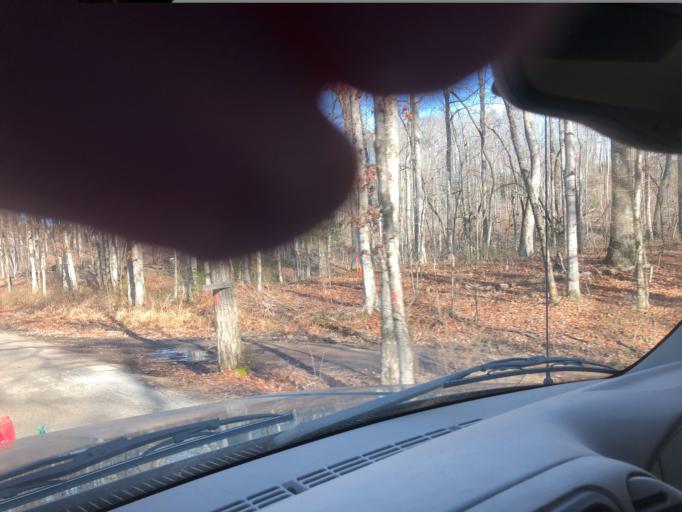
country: US
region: Tennessee
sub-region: Putnam County
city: Monterey
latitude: 35.9951
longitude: -85.2776
